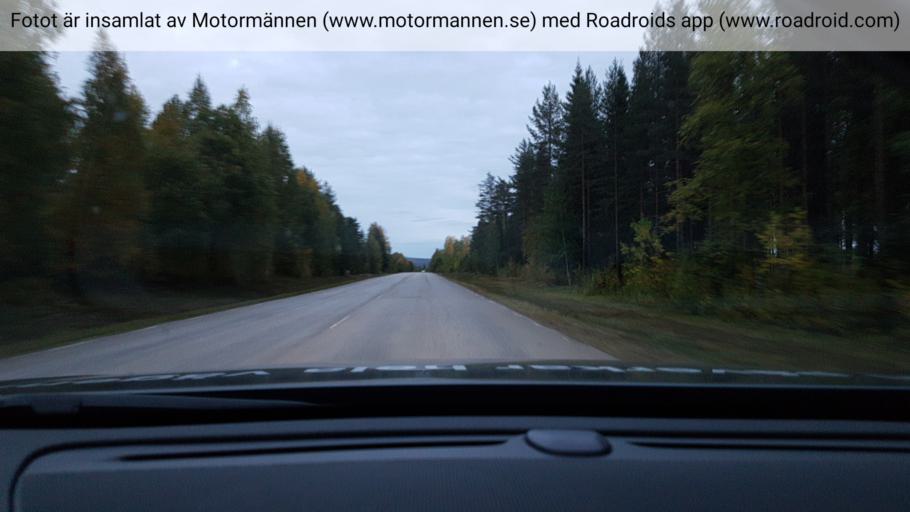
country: SE
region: Norrbotten
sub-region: Alvsbyns Kommun
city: AElvsbyn
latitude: 65.8469
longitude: 20.4687
